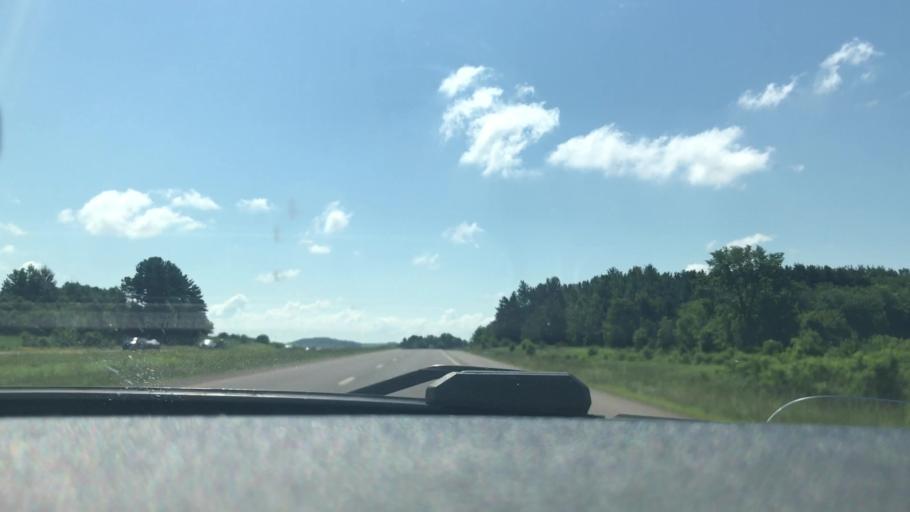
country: US
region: Wisconsin
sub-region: Chippewa County
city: Bloomer
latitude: 45.0779
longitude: -91.4791
